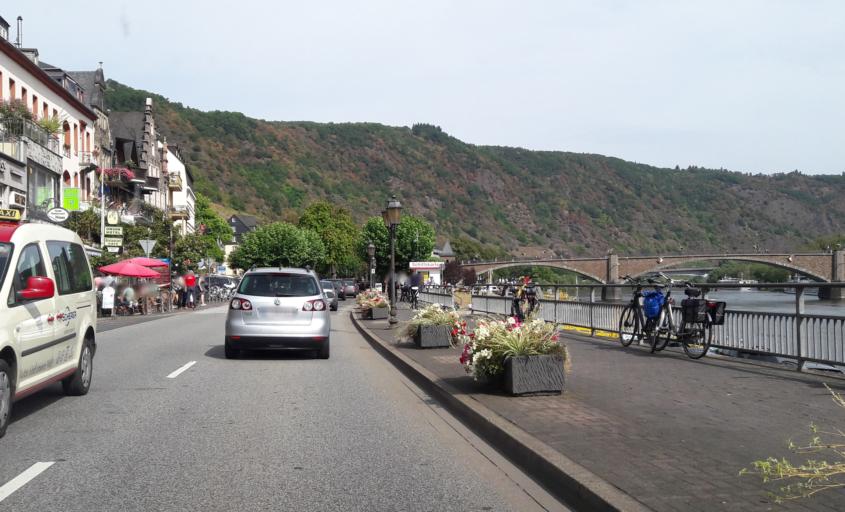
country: DE
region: Rheinland-Pfalz
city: Cochem
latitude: 50.1445
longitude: 7.1674
